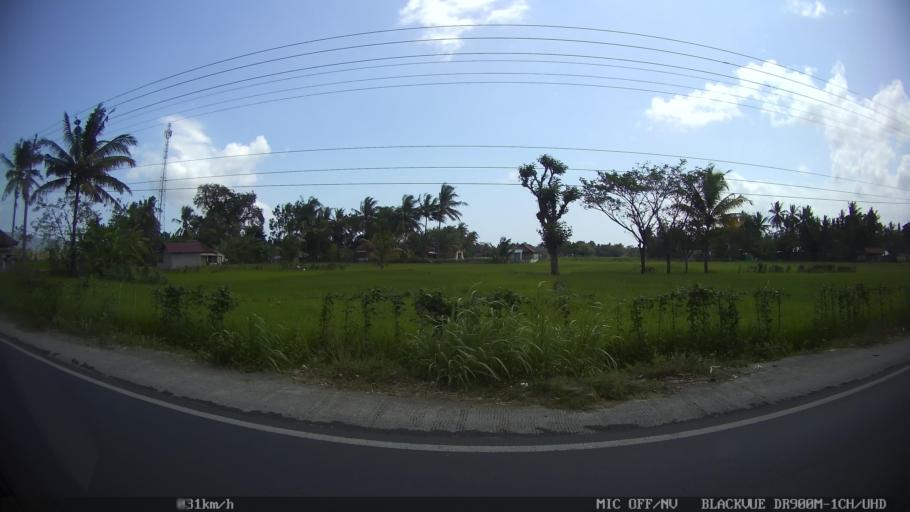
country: ID
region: Daerah Istimewa Yogyakarta
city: Pundong
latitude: -7.9301
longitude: 110.3736
